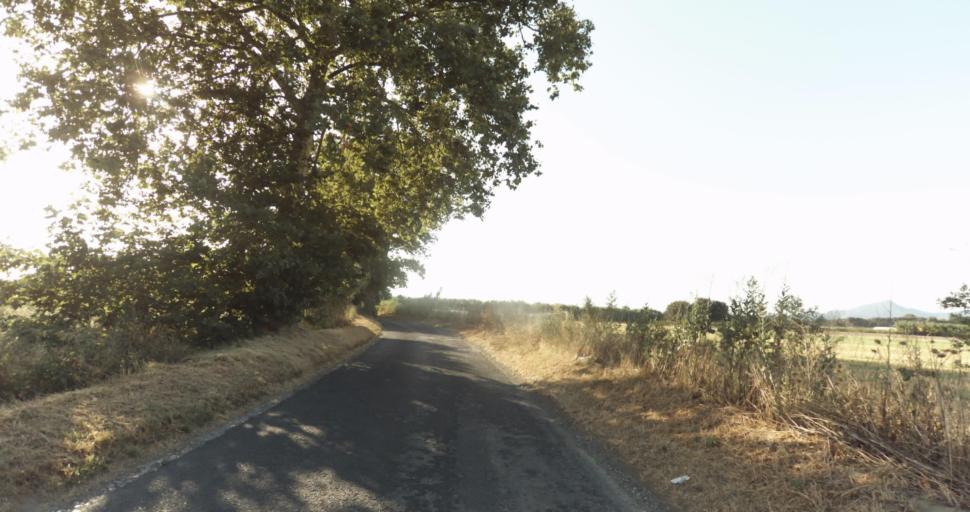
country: FR
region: Languedoc-Roussillon
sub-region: Departement des Pyrenees-Orientales
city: Latour-Bas-Elne
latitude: 42.5962
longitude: 3.0180
